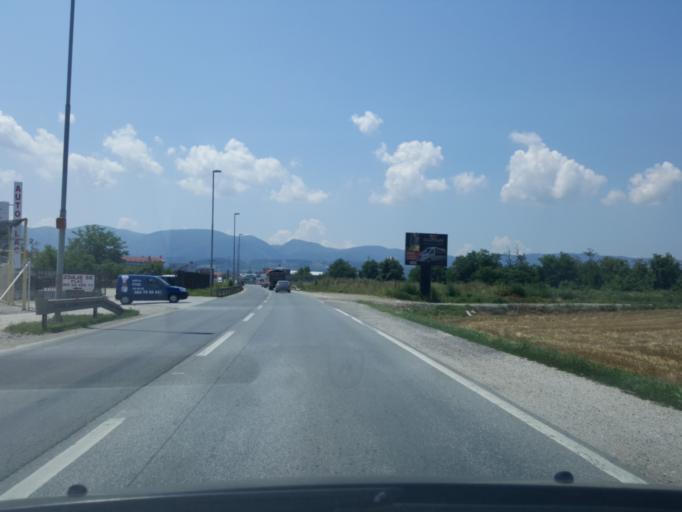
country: RS
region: Central Serbia
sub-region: Moravicki Okrug
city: Cacak
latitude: 43.8948
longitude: 20.3882
